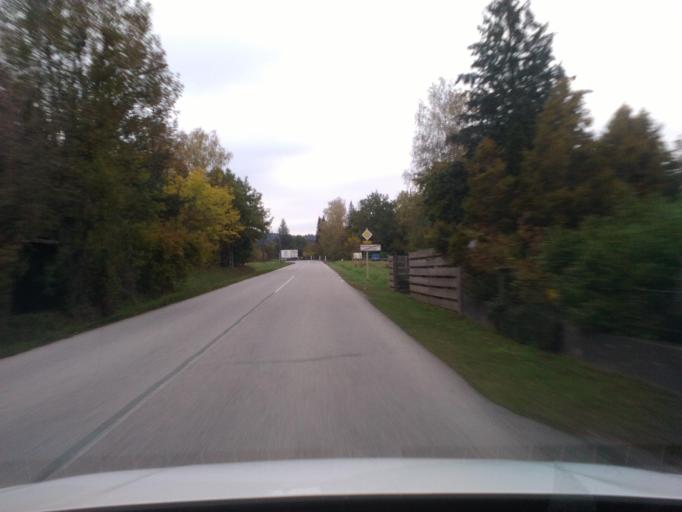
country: FR
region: Lorraine
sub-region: Departement des Vosges
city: Ban-de-Laveline
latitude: 48.3115
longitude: 7.0882
